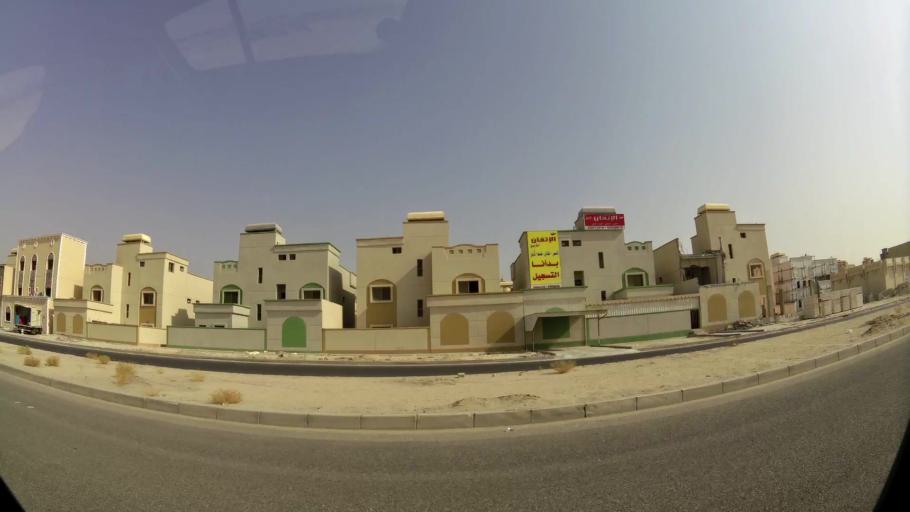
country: KW
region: Muhafazat al Jahra'
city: Al Jahra'
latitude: 29.3459
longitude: 47.7633
